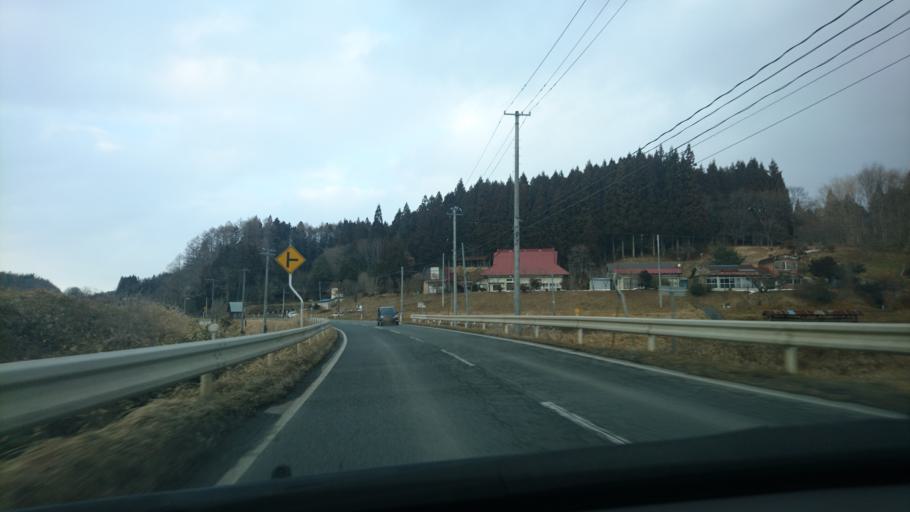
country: JP
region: Iwate
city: Ichinoseki
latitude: 38.9612
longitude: 141.3352
